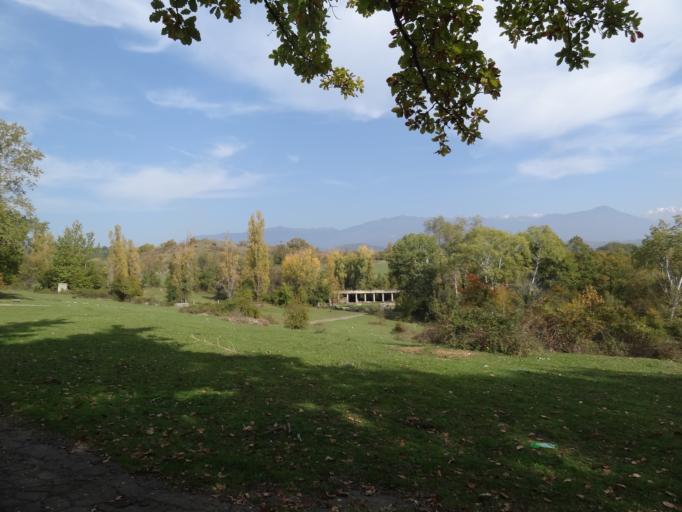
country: GE
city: Gantiadi
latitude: 43.3974
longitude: 40.0348
